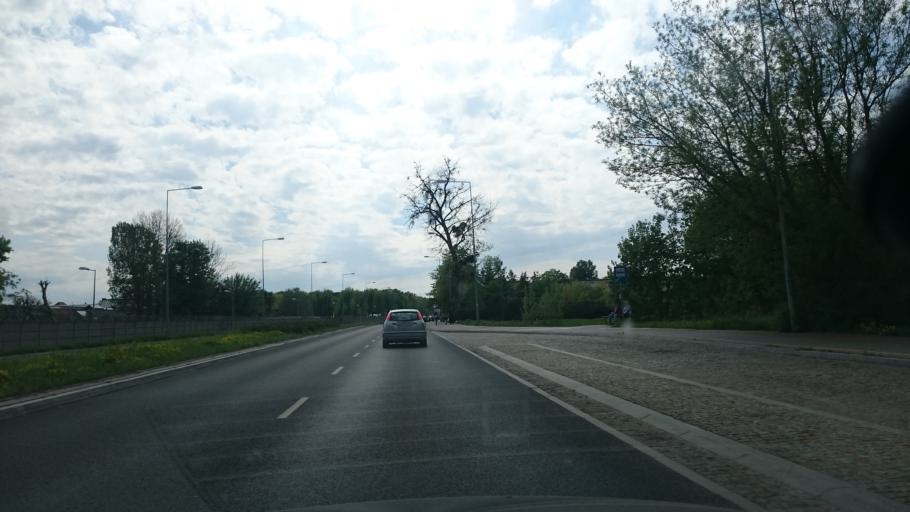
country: PL
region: Kujawsko-Pomorskie
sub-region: Grudziadz
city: Grudziadz
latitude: 53.4750
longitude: 18.7752
